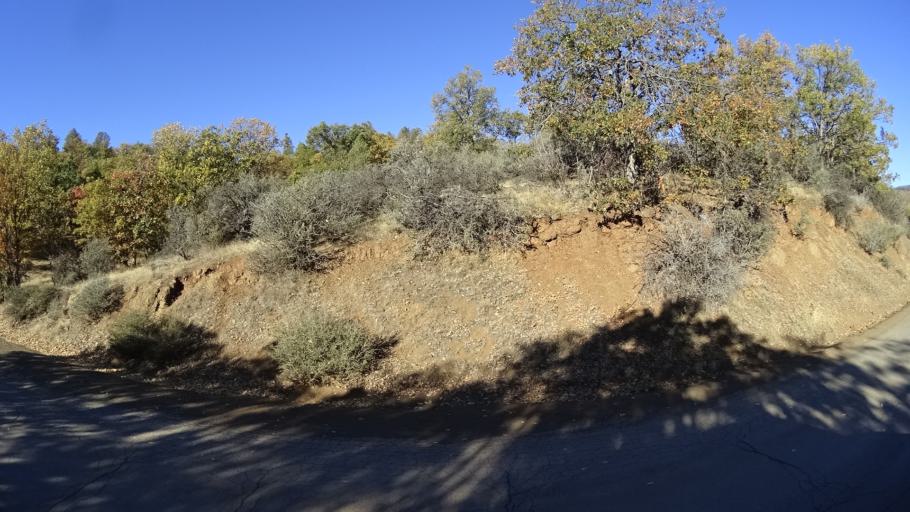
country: US
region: California
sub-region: Siskiyou County
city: Montague
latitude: 41.9671
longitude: -122.4384
